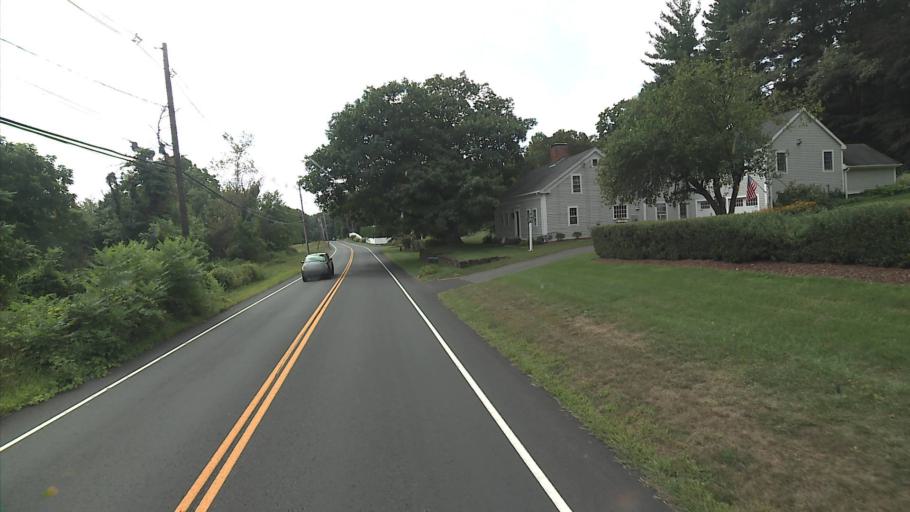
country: US
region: Connecticut
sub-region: Hartford County
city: Weatogue
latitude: 41.8216
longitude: -72.7688
